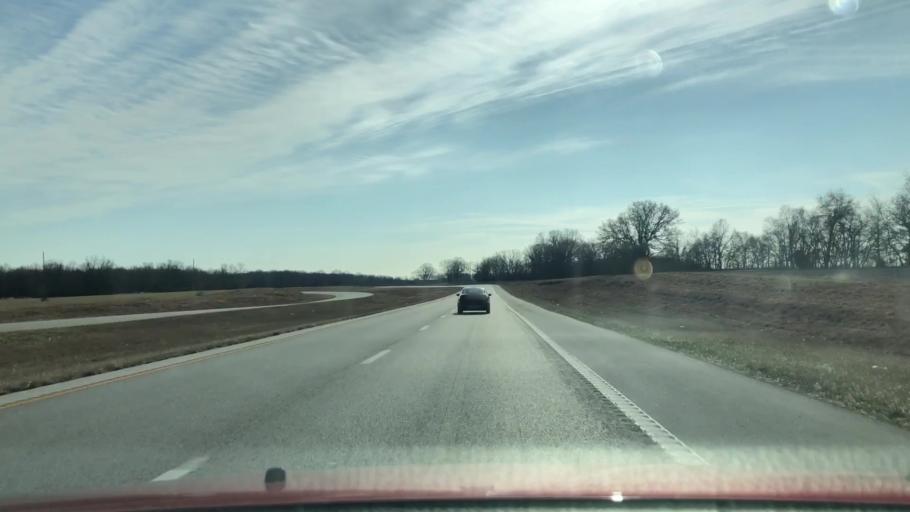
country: US
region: Missouri
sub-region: Webster County
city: Seymour
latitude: 37.1358
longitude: -92.7433
